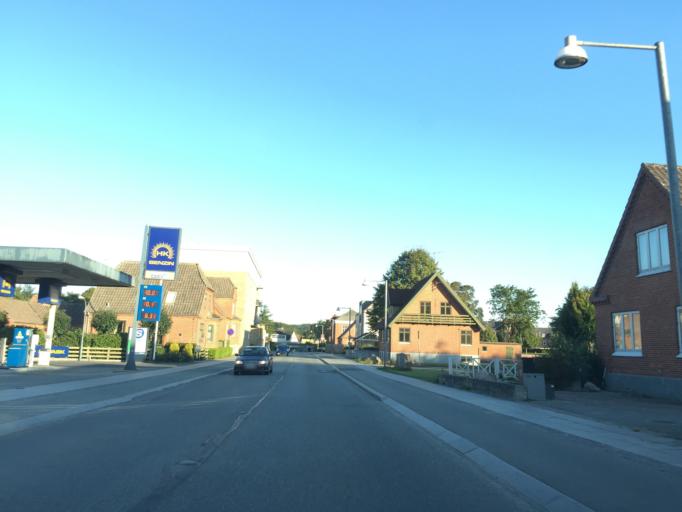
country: DK
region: Central Jutland
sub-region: Viborg Kommune
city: Bjerringbro
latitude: 56.3723
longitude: 9.6582
